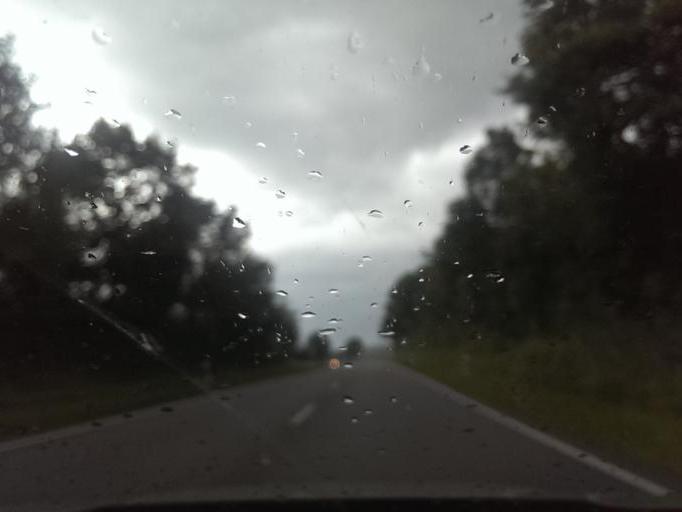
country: DE
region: North Rhine-Westphalia
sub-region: Regierungsbezirk Detmold
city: Steinheim
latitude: 51.8961
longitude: 9.0835
